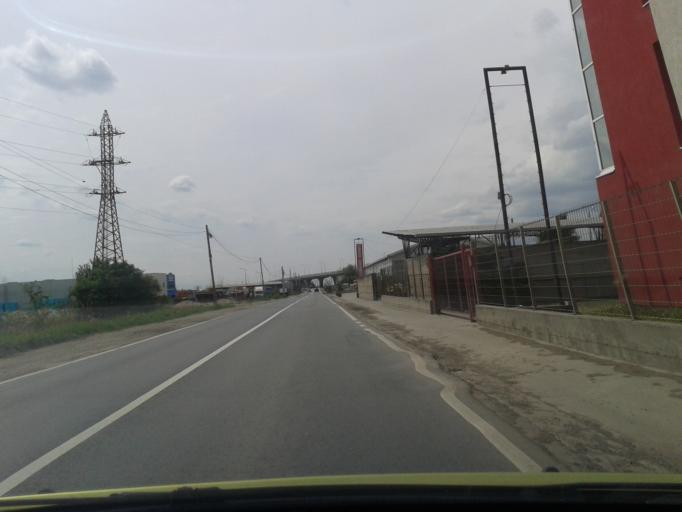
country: RO
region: Alba
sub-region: Municipiul Alba Iulia
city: Alba Iulia
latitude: 46.0540
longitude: 23.5748
